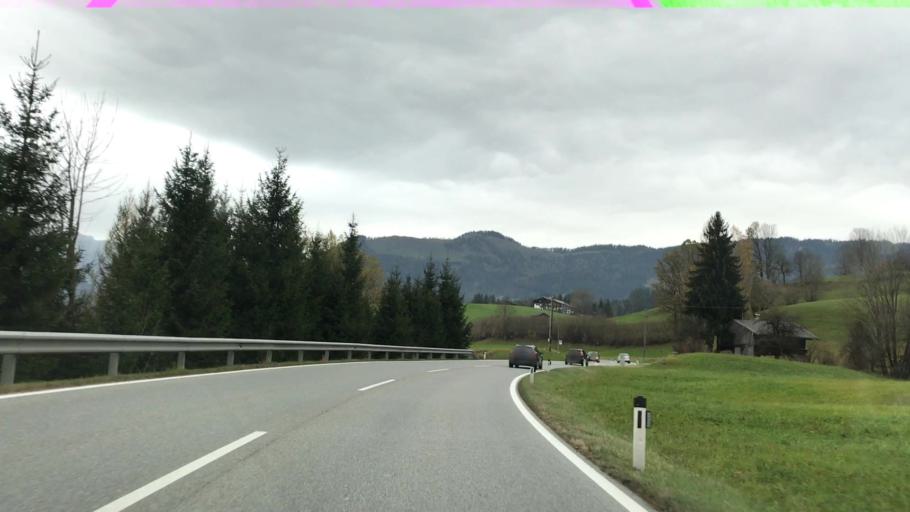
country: AT
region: Tyrol
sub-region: Politischer Bezirk Kitzbuhel
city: Kossen
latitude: 47.6528
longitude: 12.4308
